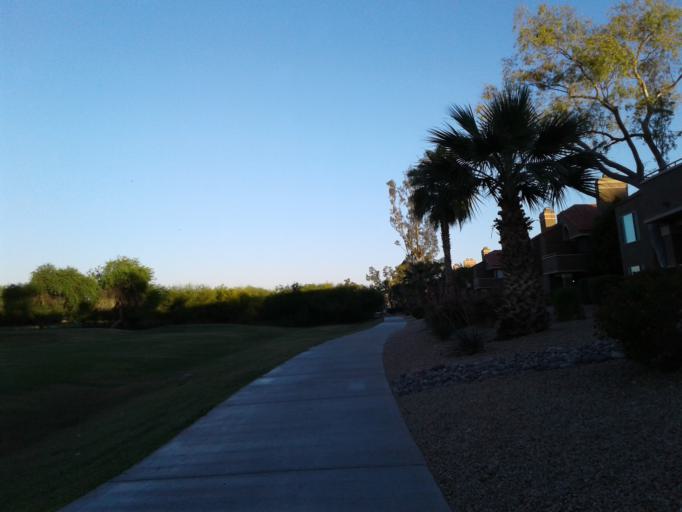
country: US
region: Arizona
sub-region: Maricopa County
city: Paradise Valley
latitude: 33.5847
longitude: -111.9718
